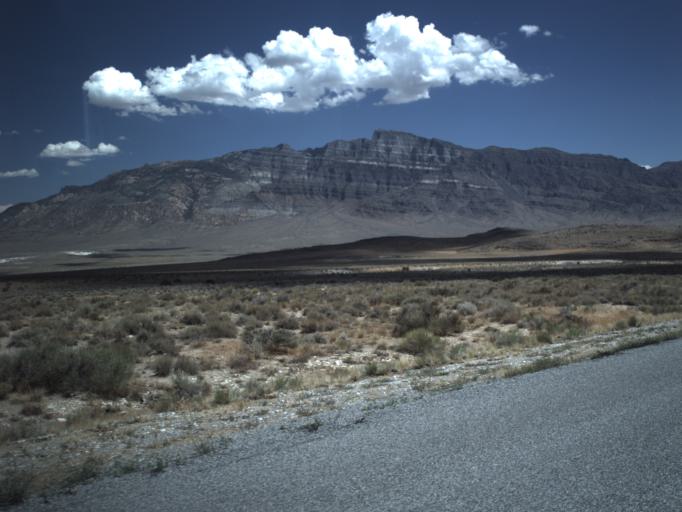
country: US
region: Utah
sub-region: Beaver County
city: Milford
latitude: 39.0872
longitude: -113.5421
